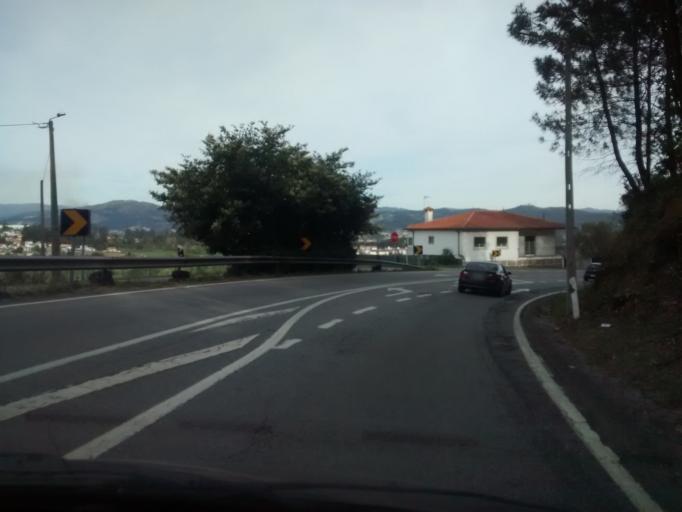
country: PT
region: Braga
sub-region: Guimaraes
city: Brito
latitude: 41.5044
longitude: -8.3660
